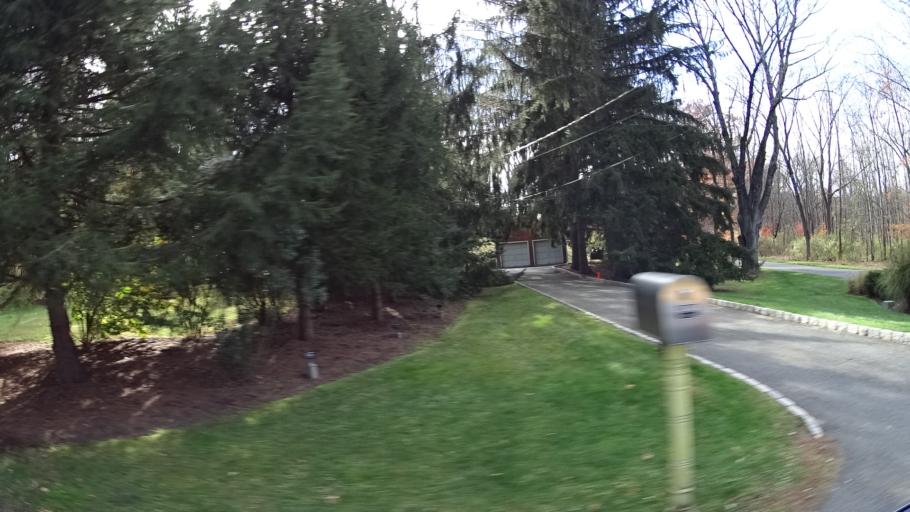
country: US
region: New Jersey
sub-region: Morris County
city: Mendham
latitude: 40.7754
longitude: -74.5752
